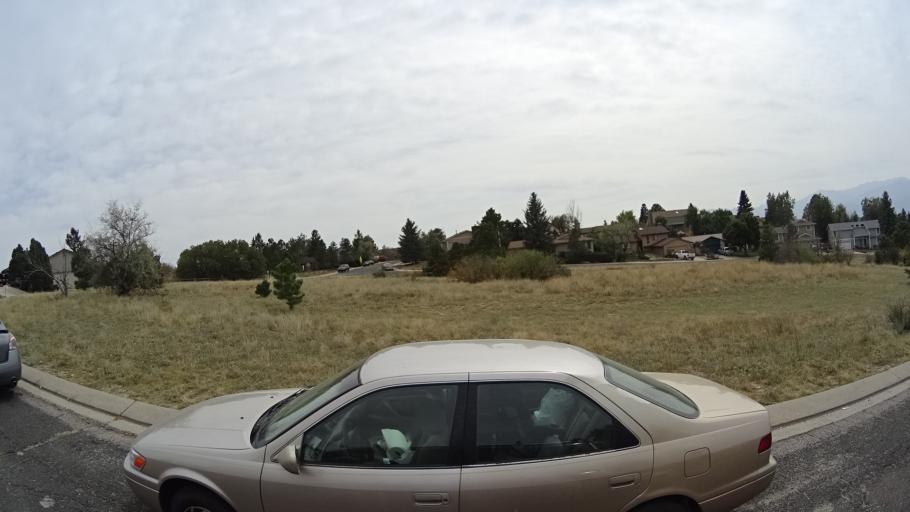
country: US
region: Colorado
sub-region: El Paso County
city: Cimarron Hills
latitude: 38.8985
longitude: -104.7278
